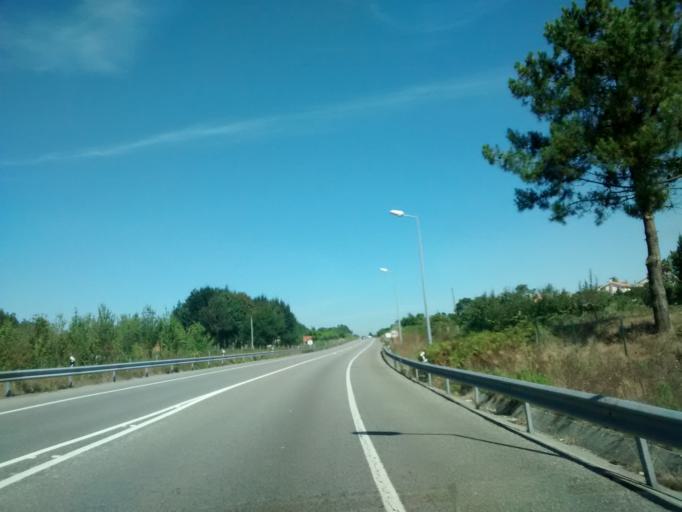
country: PT
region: Aveiro
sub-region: Anadia
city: Sangalhos
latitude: 40.4692
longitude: -8.4675
